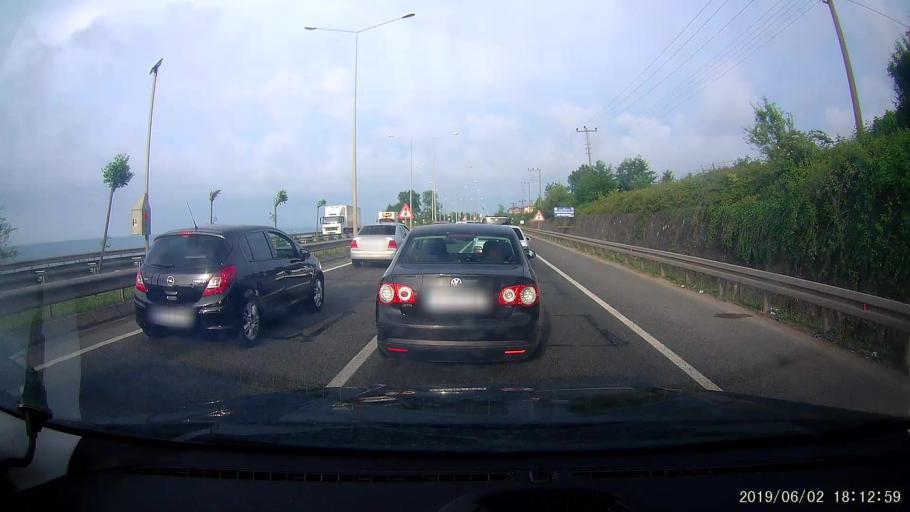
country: TR
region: Ordu
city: Unieh
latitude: 41.1067
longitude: 37.3669
